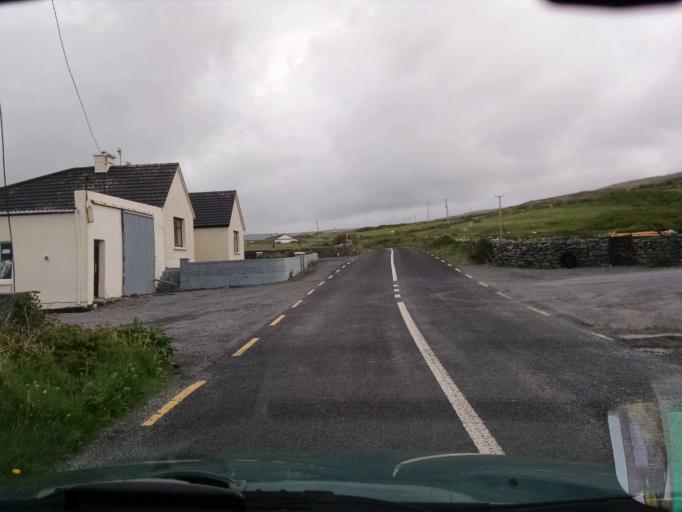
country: IE
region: Connaught
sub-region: County Galway
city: Bearna
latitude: 53.0819
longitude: -9.3325
